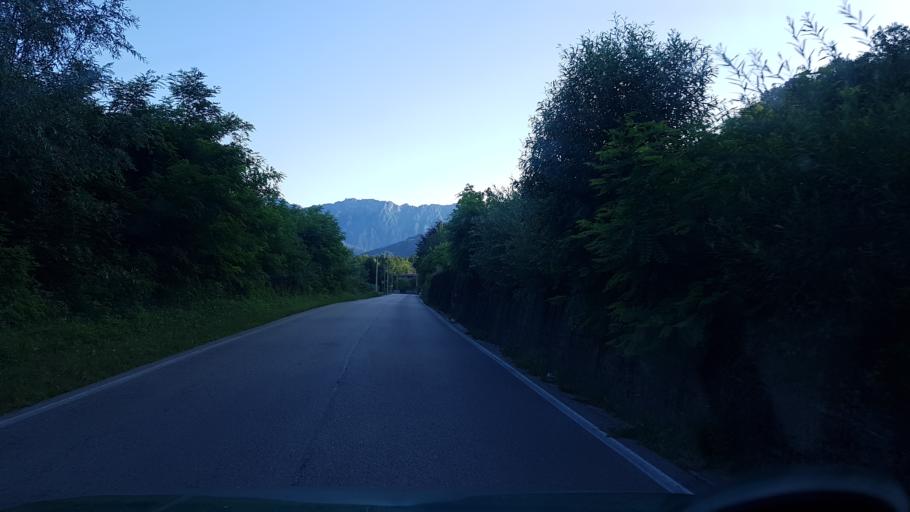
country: IT
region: Friuli Venezia Giulia
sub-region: Provincia di Udine
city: Tarcento
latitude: 46.2058
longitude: 13.2305
